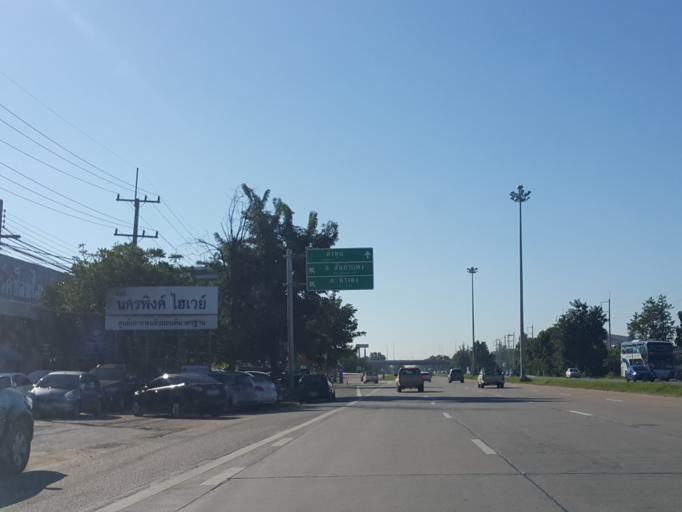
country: TH
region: Chiang Mai
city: Saraphi
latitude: 18.7583
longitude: 99.0306
